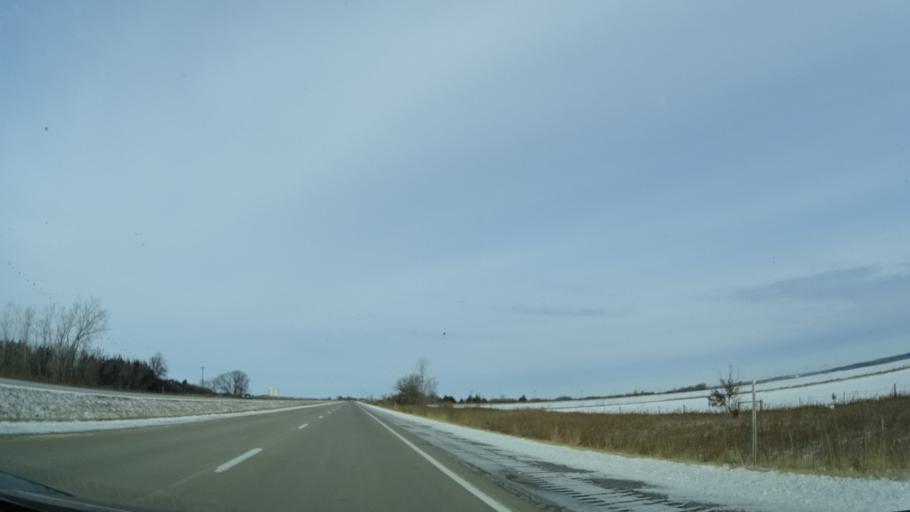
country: US
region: Iowa
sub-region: Harrison County
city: Missouri Valley
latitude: 41.5782
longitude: -95.9341
